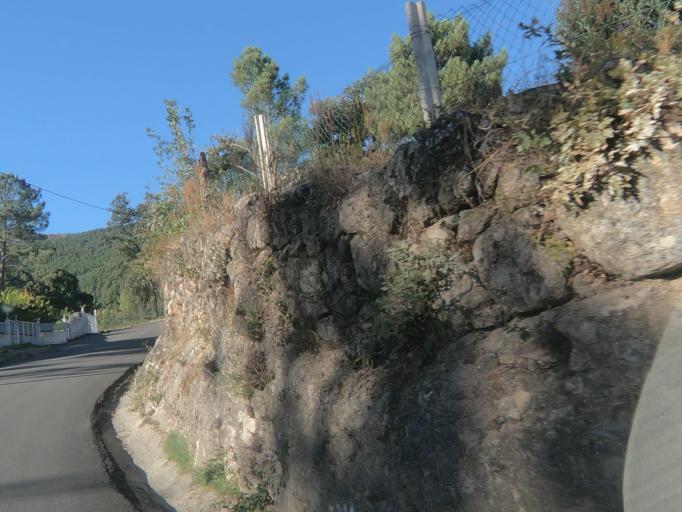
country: PT
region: Vila Real
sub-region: Vila Real
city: Vila Real
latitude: 41.3269
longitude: -7.7709
